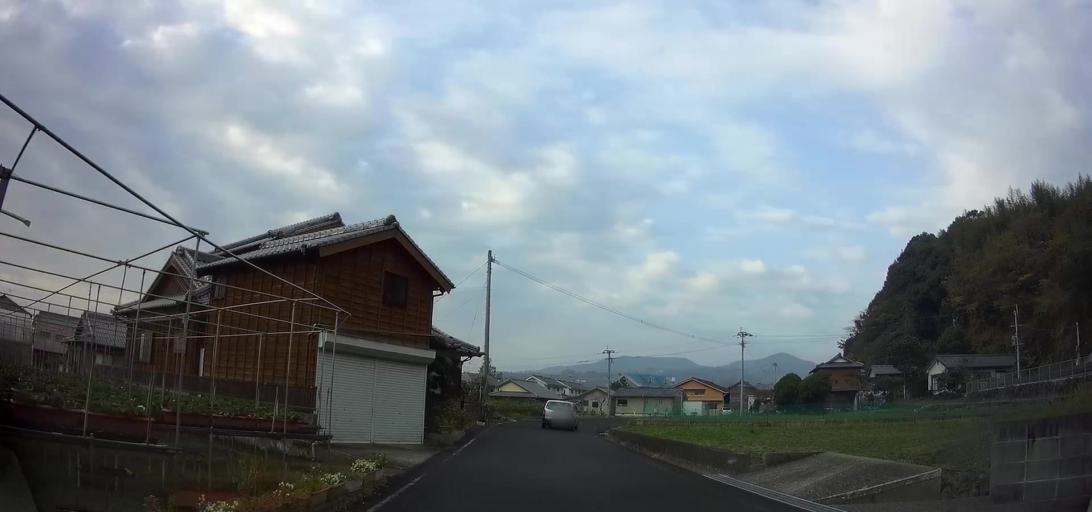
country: JP
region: Nagasaki
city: Shimabara
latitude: 32.6575
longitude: 130.2515
